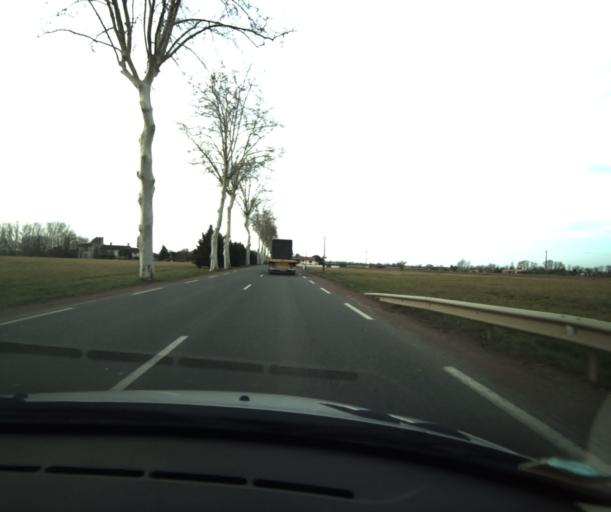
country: FR
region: Midi-Pyrenees
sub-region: Departement du Tarn-et-Garonne
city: Saint-Porquier
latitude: 44.0165
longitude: 1.1640
